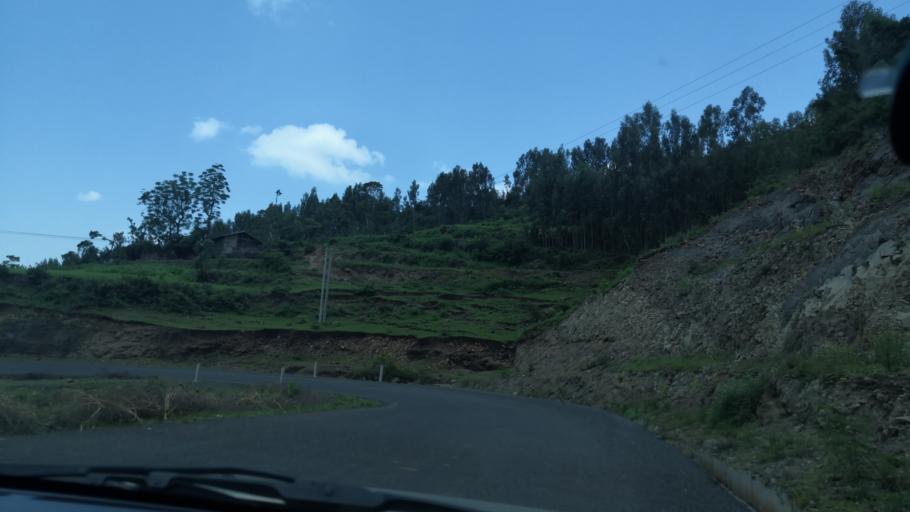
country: ET
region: Amhara
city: Abomsa
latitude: 10.3128
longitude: 39.8751
